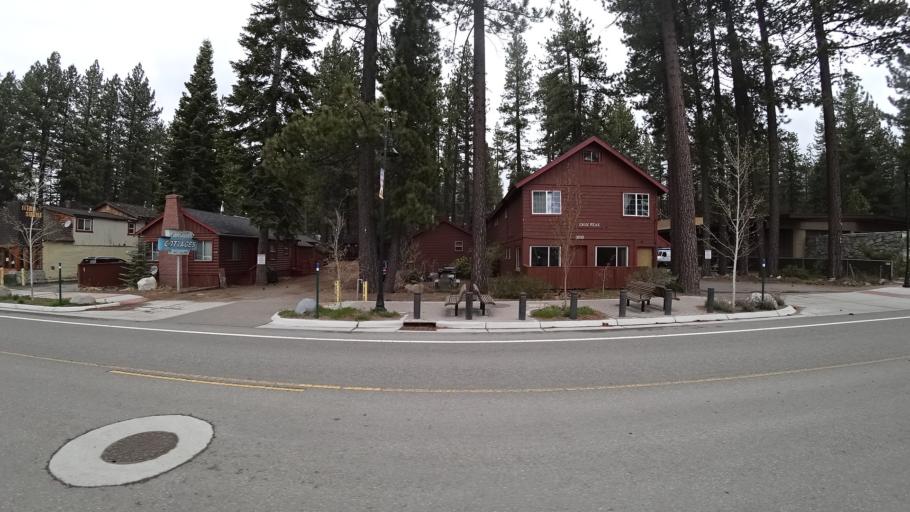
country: US
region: California
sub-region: Placer County
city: Kings Beach
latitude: 39.2375
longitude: -120.0283
